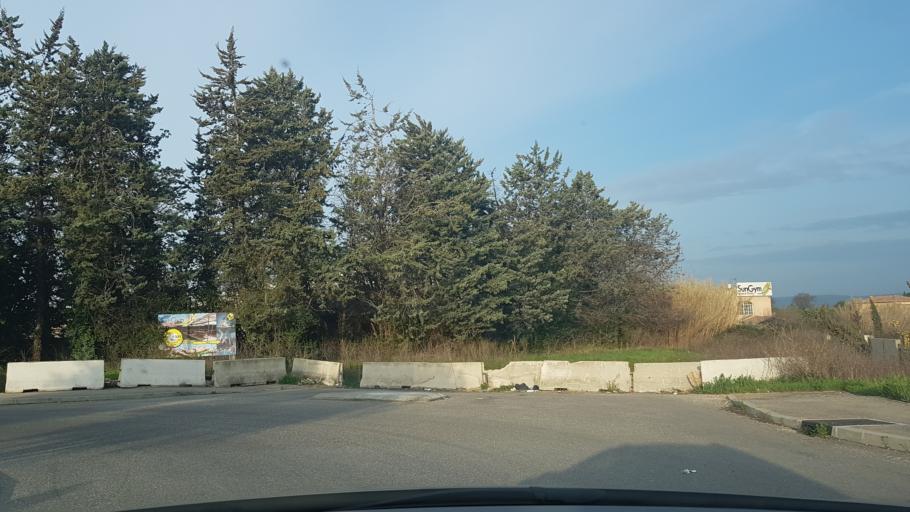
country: FR
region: Provence-Alpes-Cote d'Azur
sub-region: Departement des Bouches-du-Rhone
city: Bouc-Bel-Air
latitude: 43.4984
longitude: 5.3798
